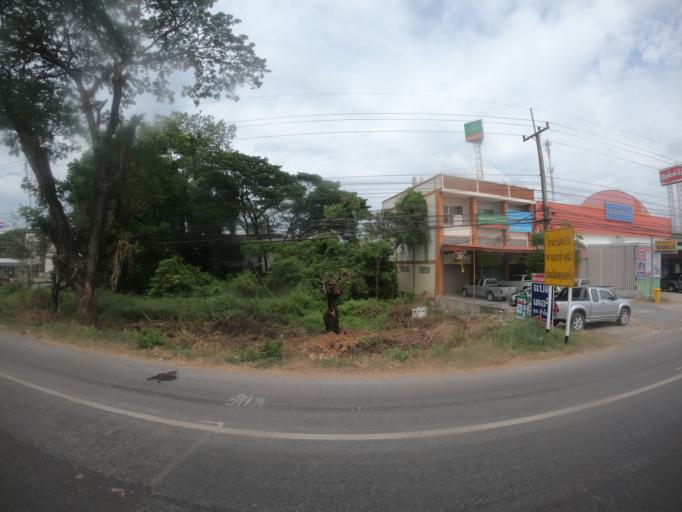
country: TH
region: Roi Et
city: Roi Et
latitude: 16.0688
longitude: 103.6061
